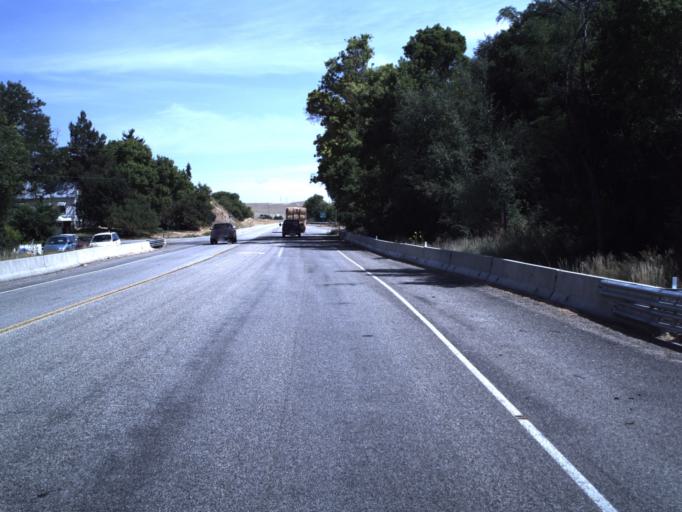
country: US
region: Utah
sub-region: Cache County
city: Mendon
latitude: 41.7954
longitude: -112.0411
